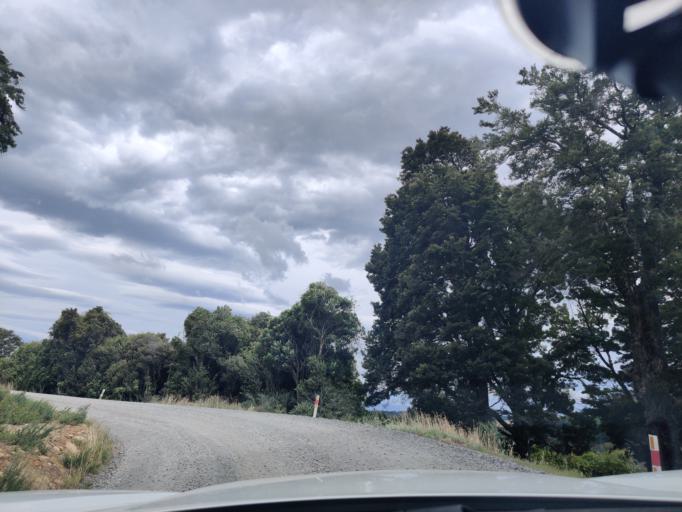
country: NZ
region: Wellington
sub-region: Masterton District
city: Masterton
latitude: -41.0400
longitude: 175.4035
